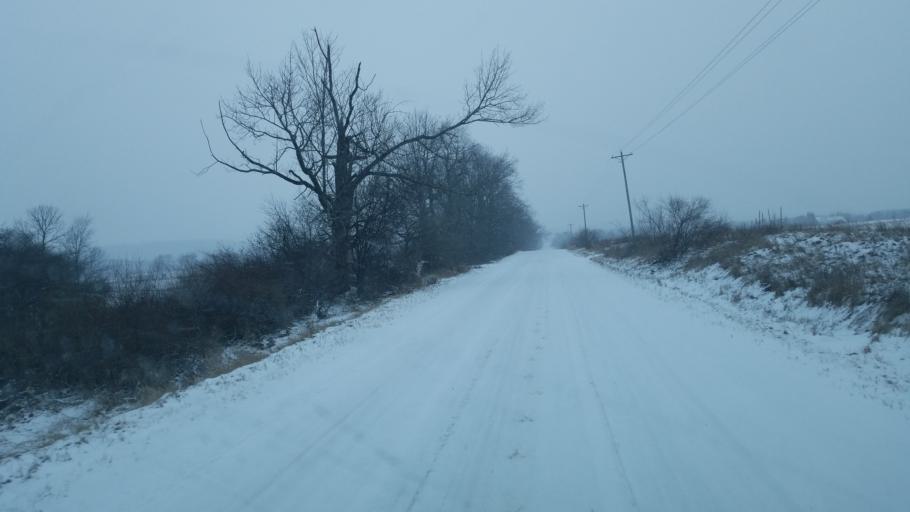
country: US
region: Michigan
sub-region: Osceola County
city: Reed City
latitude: 43.8289
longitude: -85.4071
